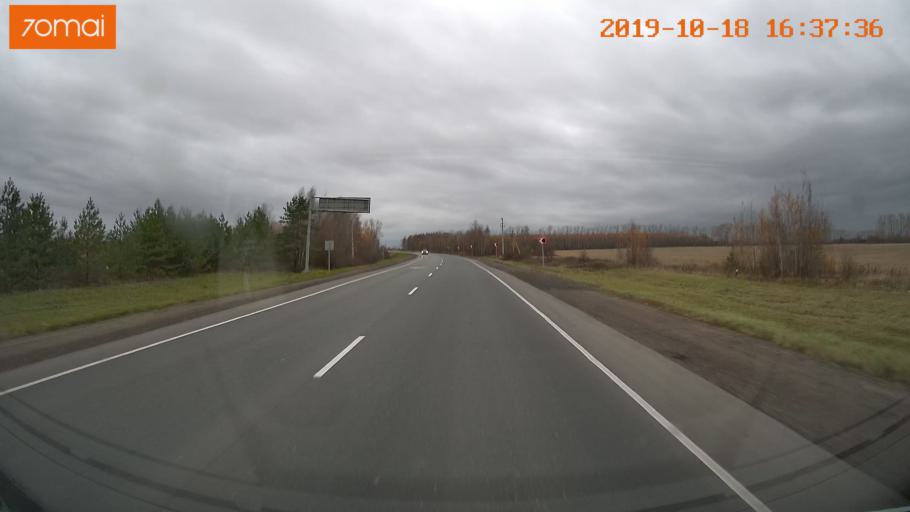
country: RU
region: Vladimir
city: Suzdal'
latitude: 56.4242
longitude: 40.4765
